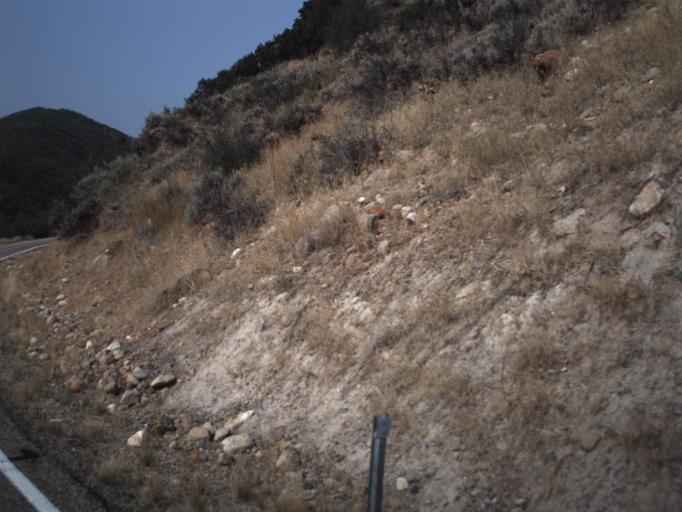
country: US
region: Utah
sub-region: Summit County
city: Summit Park
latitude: 40.8532
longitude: -111.5939
